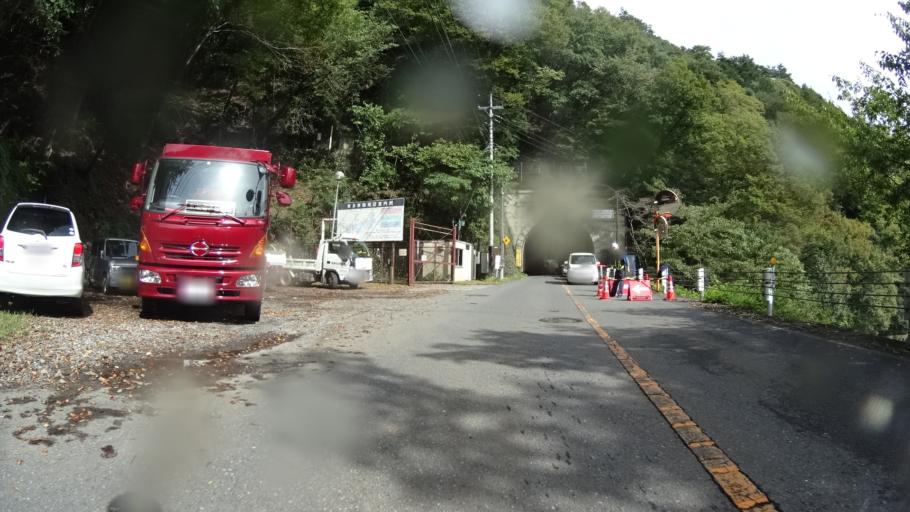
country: JP
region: Yamanashi
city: Uenohara
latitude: 35.7825
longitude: 139.0280
